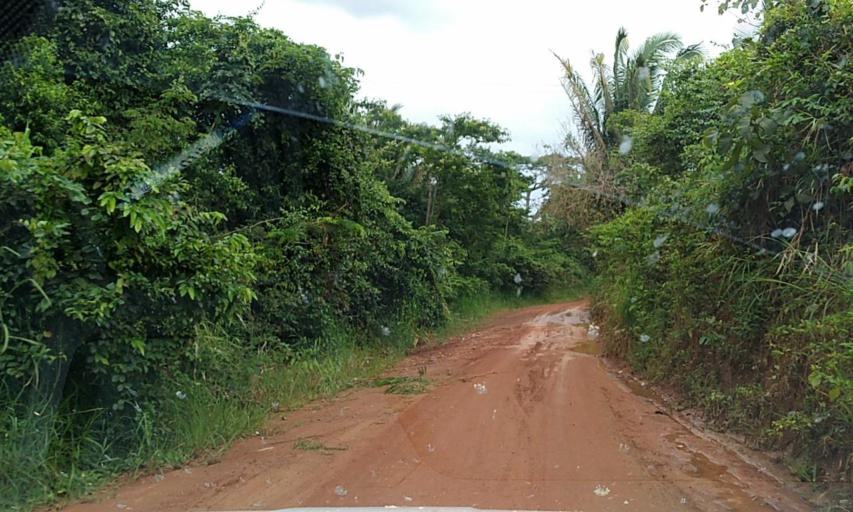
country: BR
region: Para
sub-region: Altamira
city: Altamira
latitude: -3.3079
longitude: -52.6879
